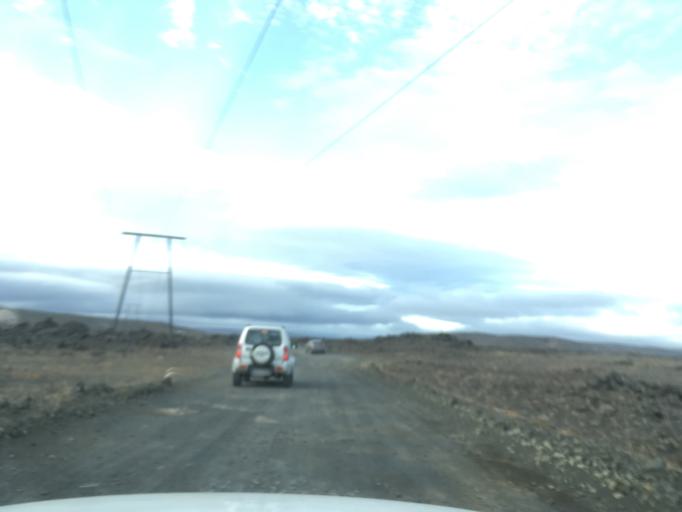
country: IS
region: South
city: Vestmannaeyjar
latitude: 64.1454
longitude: -19.1321
